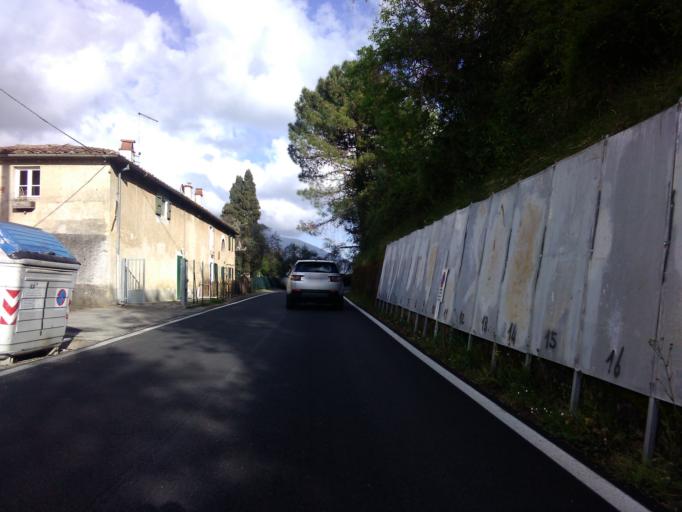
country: IT
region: Tuscany
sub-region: Provincia di Lucca
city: Piano di Mommio
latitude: 43.9499
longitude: 10.2732
